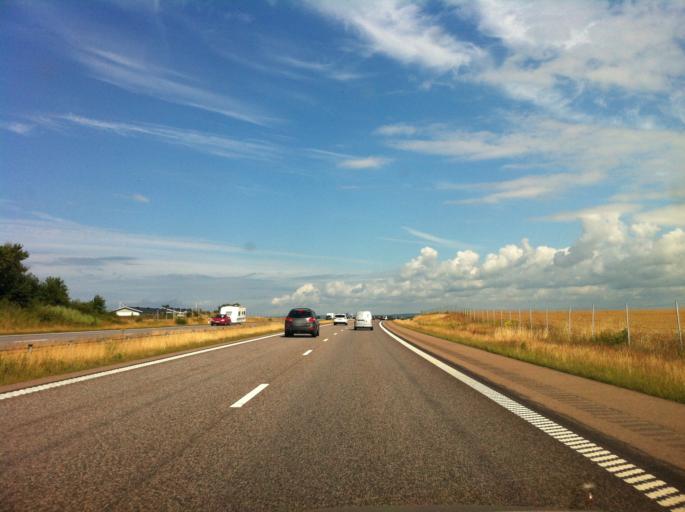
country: SE
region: Halland
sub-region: Halmstads Kommun
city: Paarp
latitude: 56.6016
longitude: 12.9267
